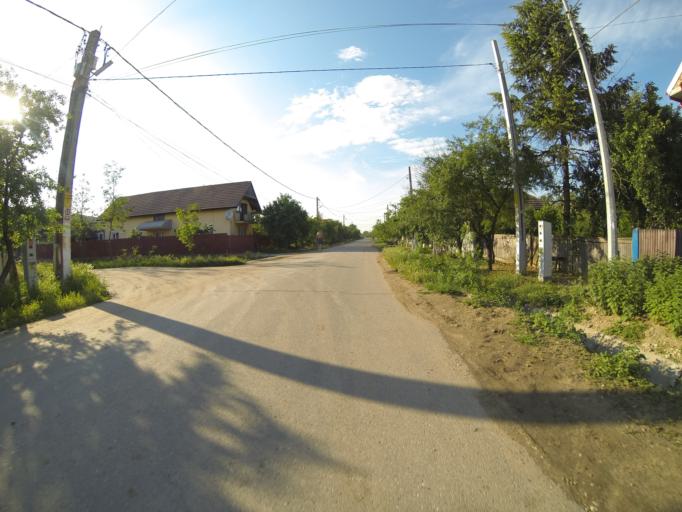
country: RO
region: Dolj
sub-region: Comuna Tuglui
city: Tuglui
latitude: 44.1805
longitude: 23.8150
